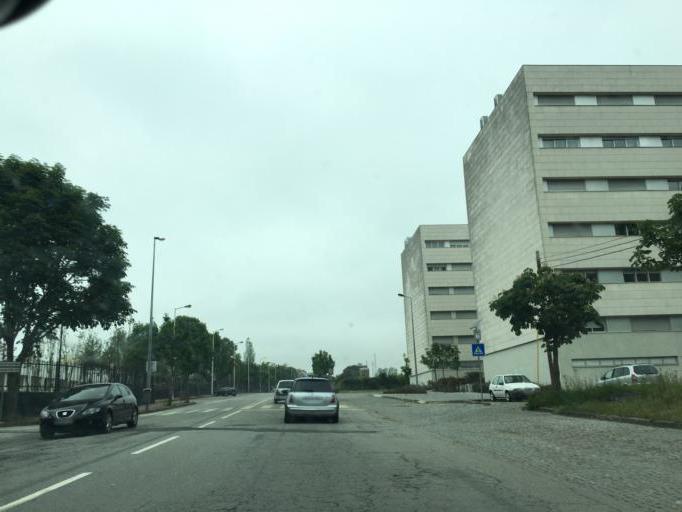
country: PT
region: Porto
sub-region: Maia
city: Anta
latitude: 41.2599
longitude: -8.6095
